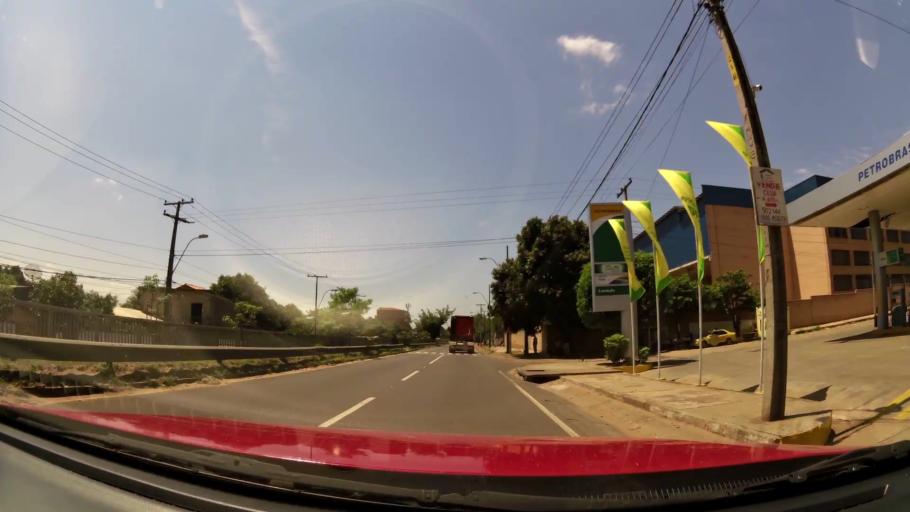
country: PY
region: Central
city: Lambare
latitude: -25.3369
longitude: -57.5818
